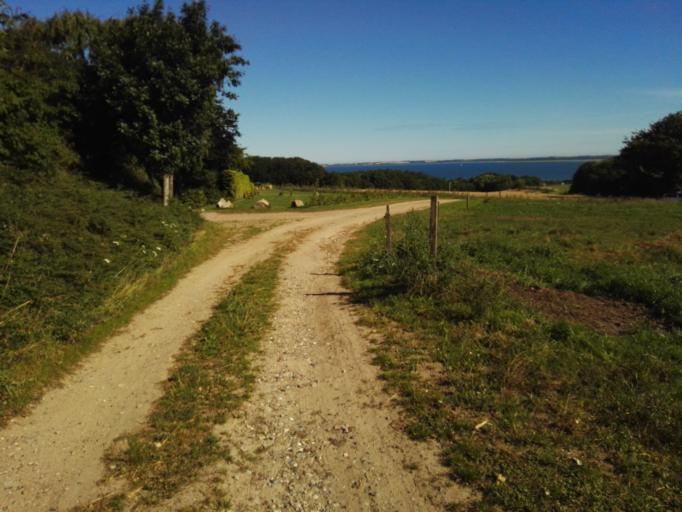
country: DK
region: Zealand
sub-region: Odsherred Kommune
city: Asnaes
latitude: 55.8385
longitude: 11.4799
